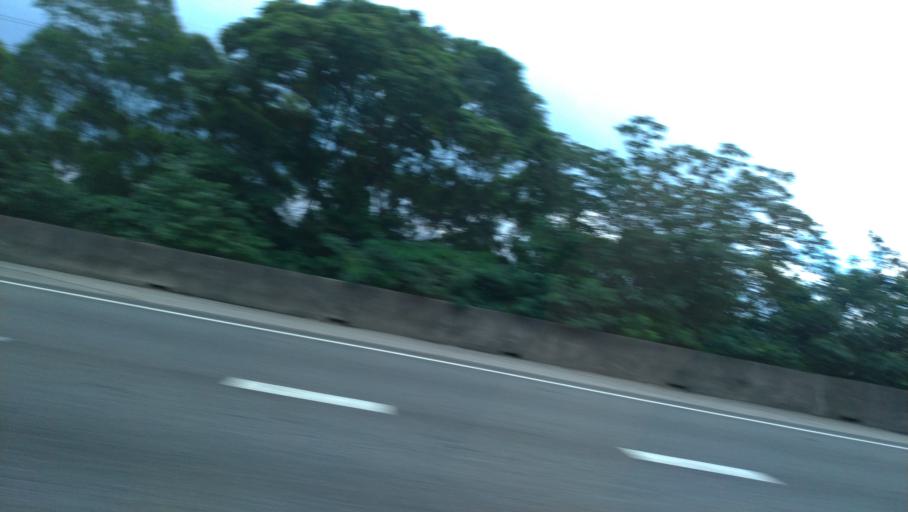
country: TW
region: Taiwan
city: Daxi
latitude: 24.9121
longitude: 121.2927
